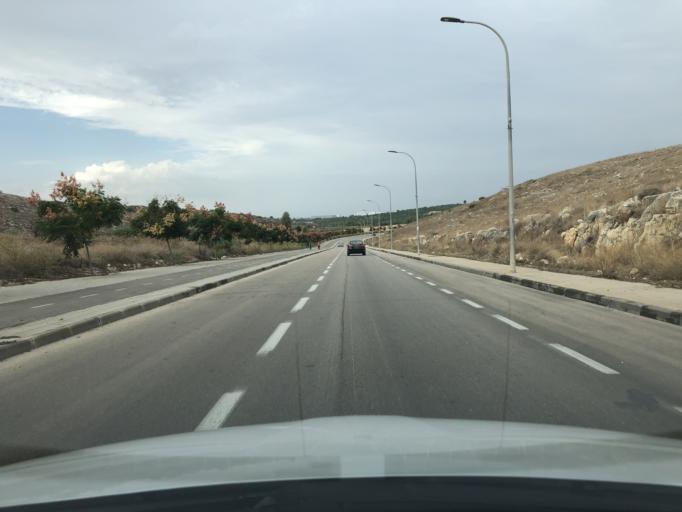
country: PS
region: West Bank
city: Al Midyah
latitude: 31.9186
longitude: 35.0003
